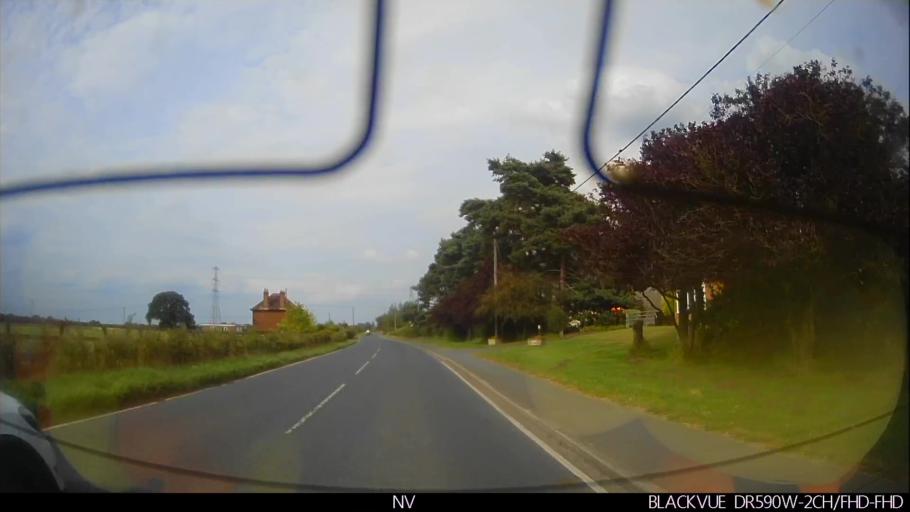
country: GB
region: England
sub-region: City of York
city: Huntington
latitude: 54.0127
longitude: -1.0511
